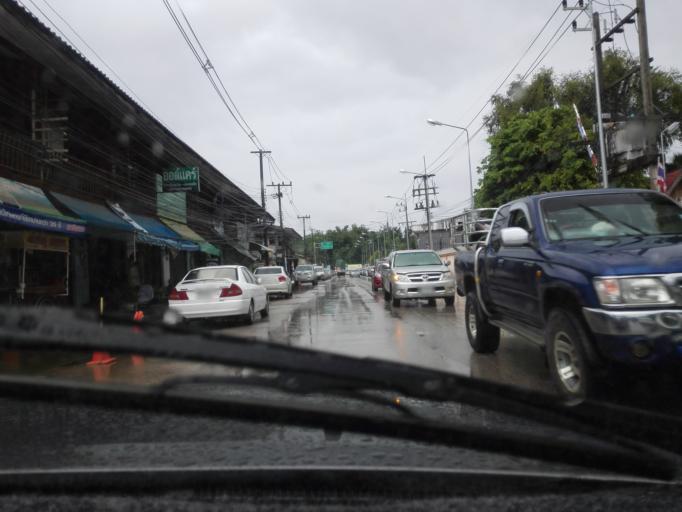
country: TH
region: Tak
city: Mae Sot
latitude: 16.7101
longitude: 98.5738
